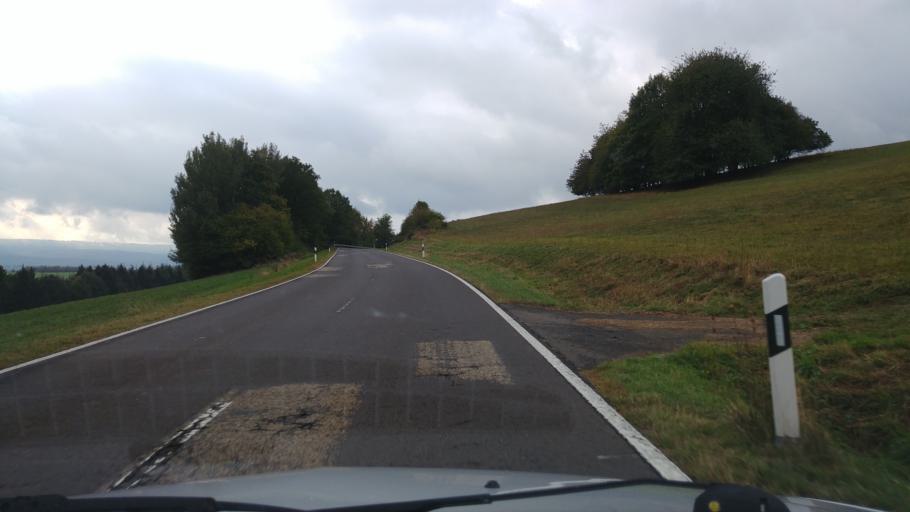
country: DE
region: Rheinland-Pfalz
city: Gornhausen
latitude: 49.8231
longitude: 7.0481
